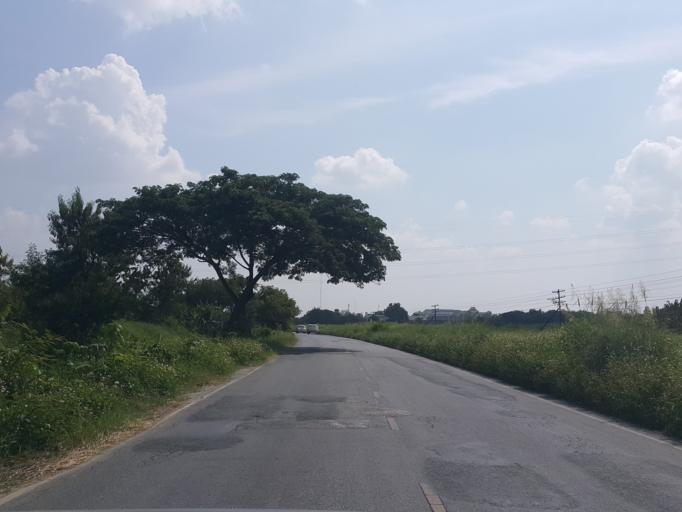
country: TH
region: Chiang Mai
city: Chiang Mai
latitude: 18.7690
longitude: 99.0174
